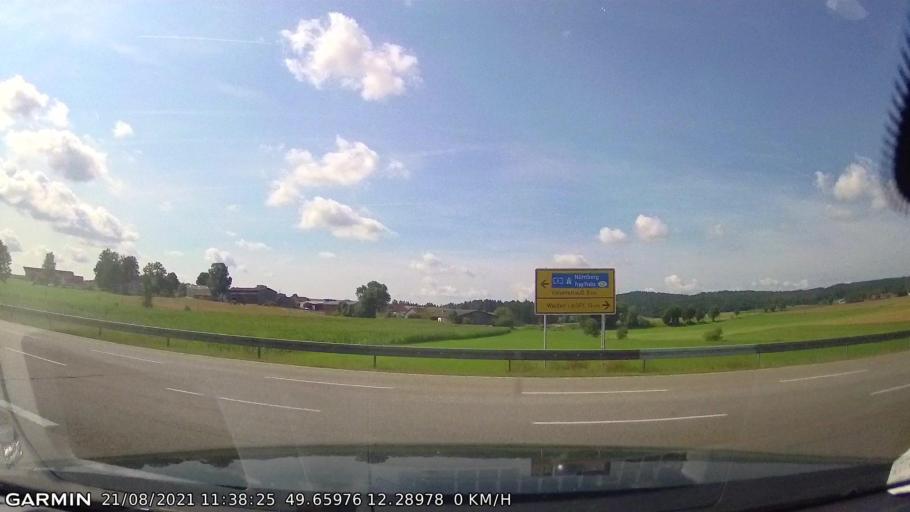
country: DE
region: Bavaria
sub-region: Upper Palatinate
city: Waldthurn
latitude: 49.6598
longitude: 12.2898
